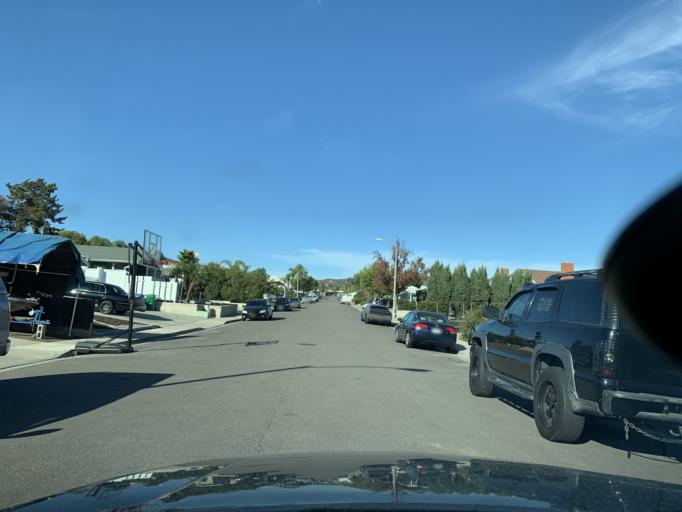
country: US
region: California
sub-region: San Diego County
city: Santee
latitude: 32.8599
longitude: -116.9774
